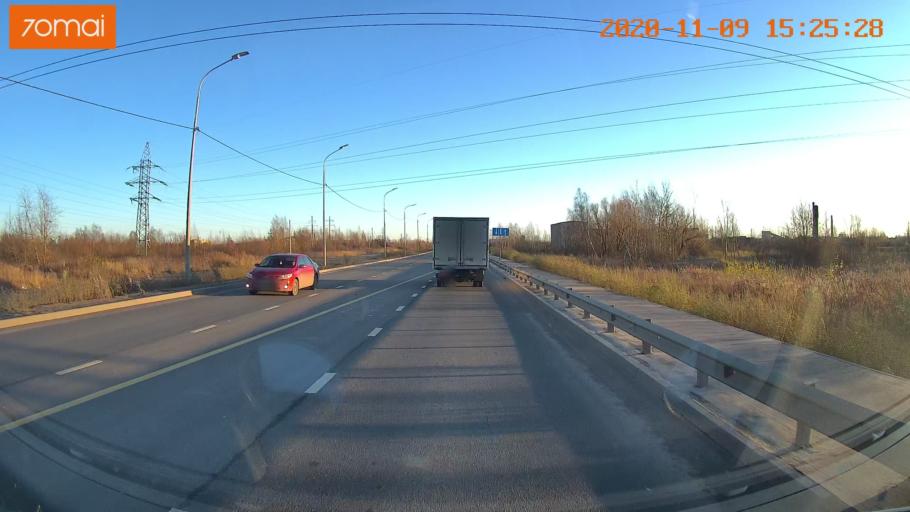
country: RU
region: Ivanovo
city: Novo-Talitsy
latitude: 56.9835
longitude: 40.9129
